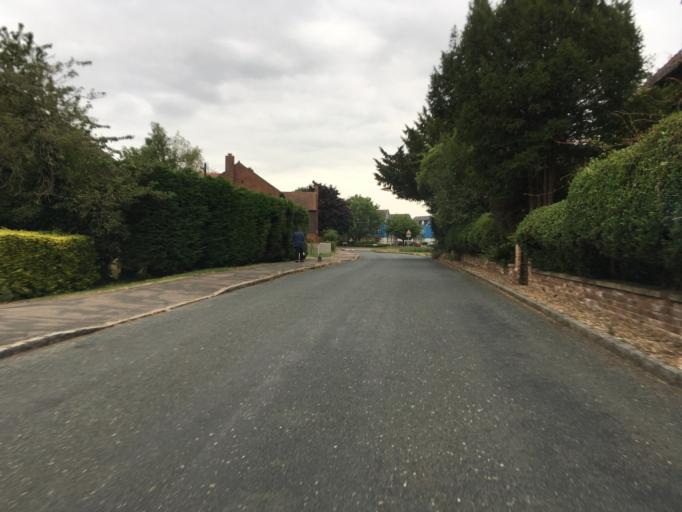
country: GB
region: England
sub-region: Milton Keynes
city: Broughton
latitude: 52.0409
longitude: -0.7037
